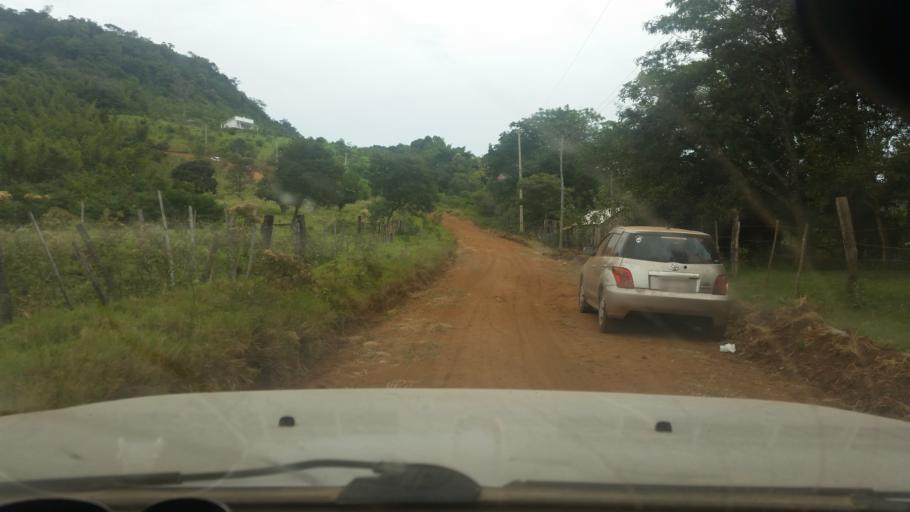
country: PY
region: Guaira
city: Independencia
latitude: -25.8049
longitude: -56.2697
